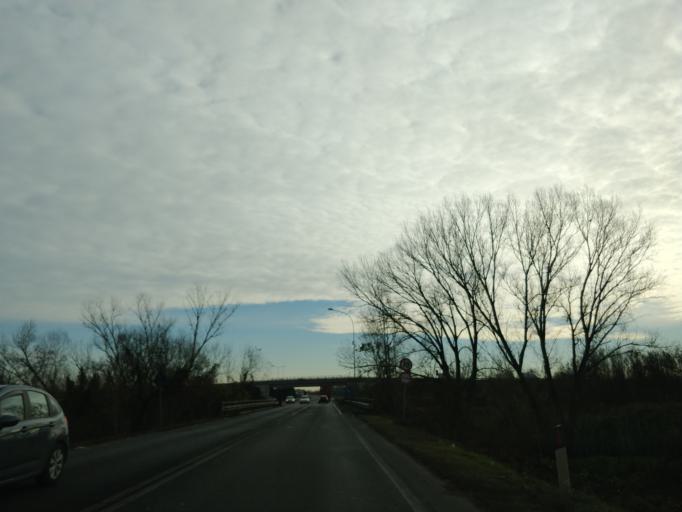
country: IT
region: Emilia-Romagna
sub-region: Provincia di Bologna
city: Castel Maggiore
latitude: 44.5902
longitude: 11.3908
